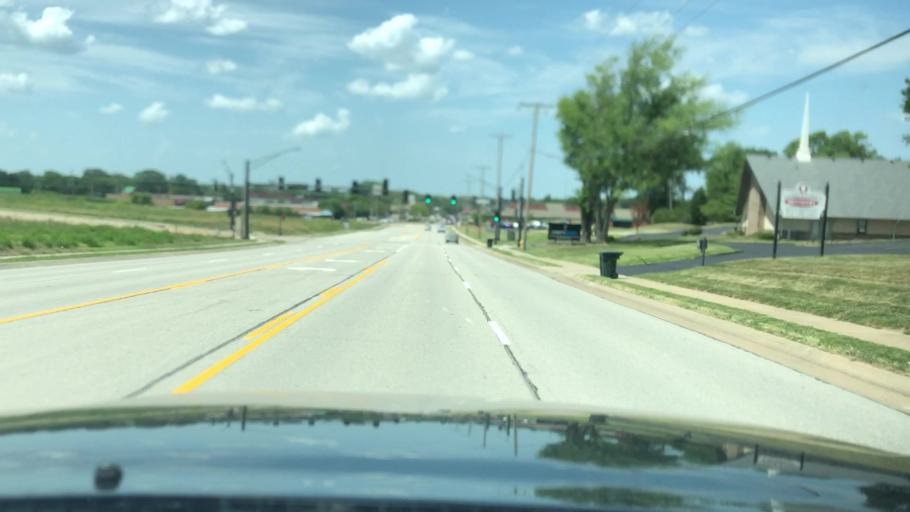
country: US
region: Missouri
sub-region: Saint Charles County
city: Saint Peters
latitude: 38.7882
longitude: -90.6206
